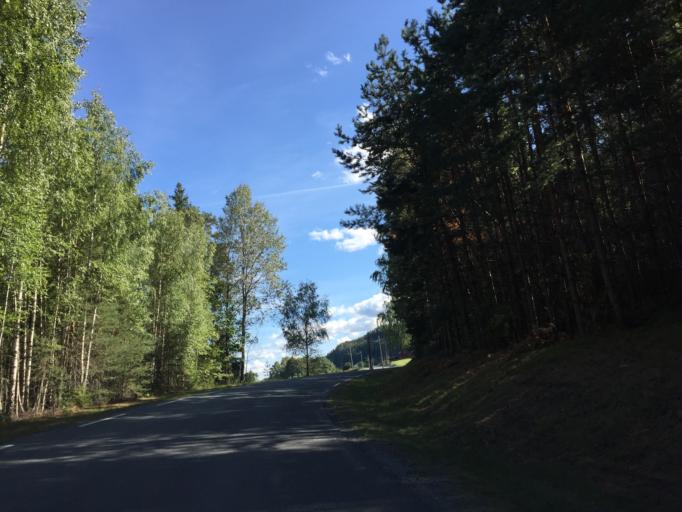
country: NO
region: Buskerud
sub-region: Ovre Eiker
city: Hokksund
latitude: 59.6935
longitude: 9.8437
